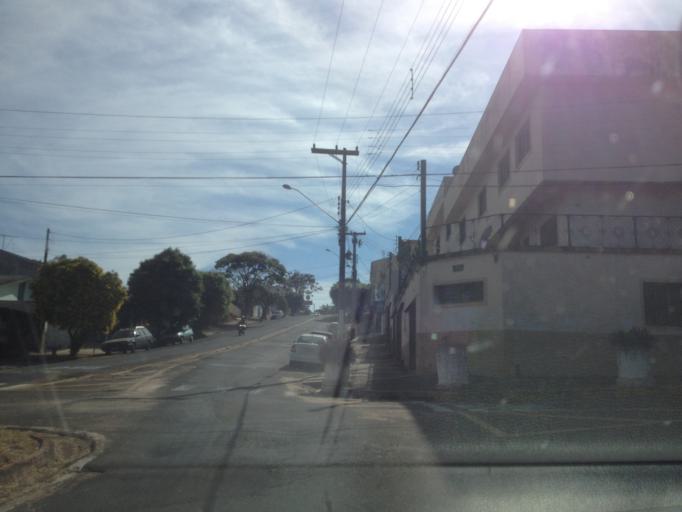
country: BR
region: Sao Paulo
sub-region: Marilia
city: Marilia
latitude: -22.2239
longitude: -49.9438
